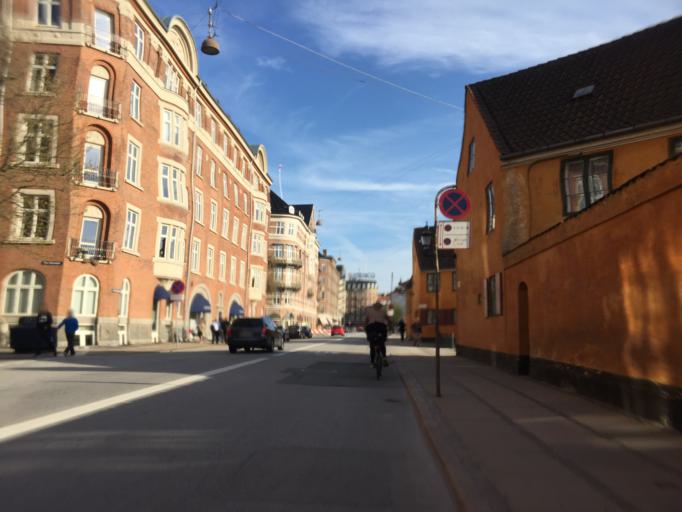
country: DK
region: Capital Region
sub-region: Kobenhavn
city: Christianshavn
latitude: 55.6894
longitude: 12.5892
